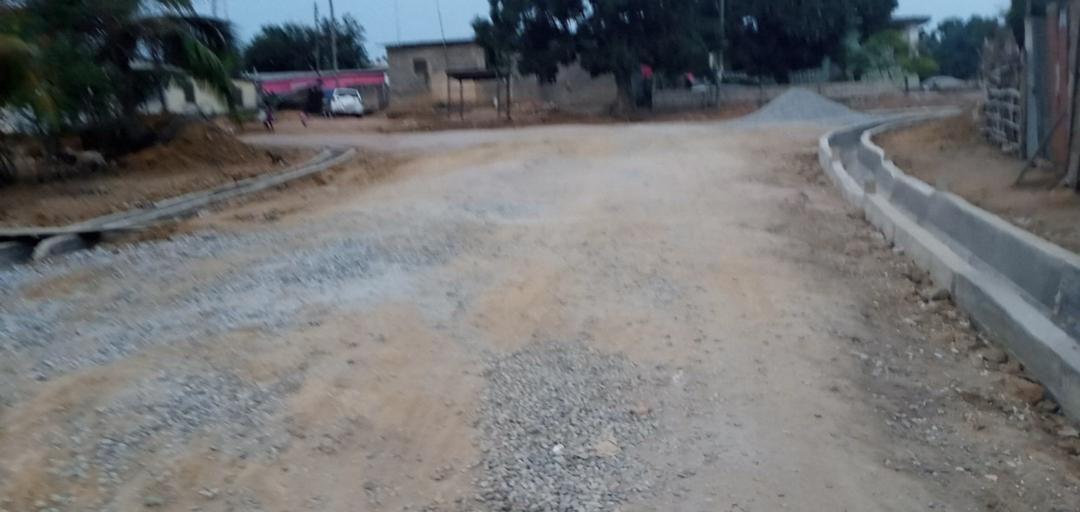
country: GH
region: Central
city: Winneba
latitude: 5.3570
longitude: -0.6273
